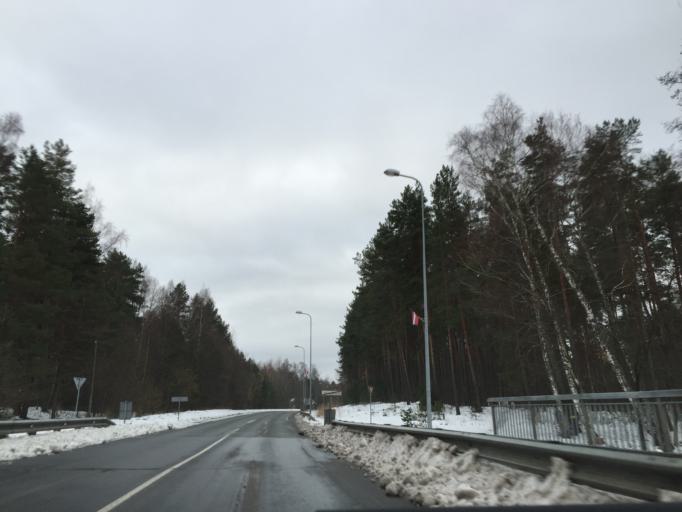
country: LV
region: Saulkrastu
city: Saulkrasti
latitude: 57.2292
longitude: 24.3934
